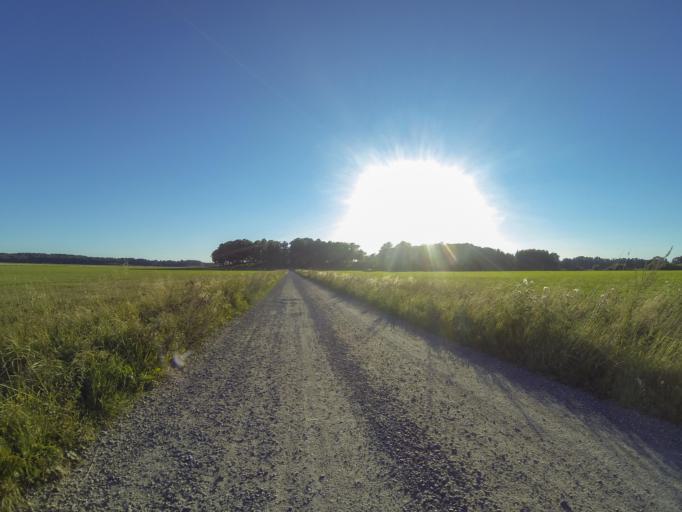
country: SE
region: Vaestmanland
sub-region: Vasteras
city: Vasteras
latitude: 59.5711
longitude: 16.6461
